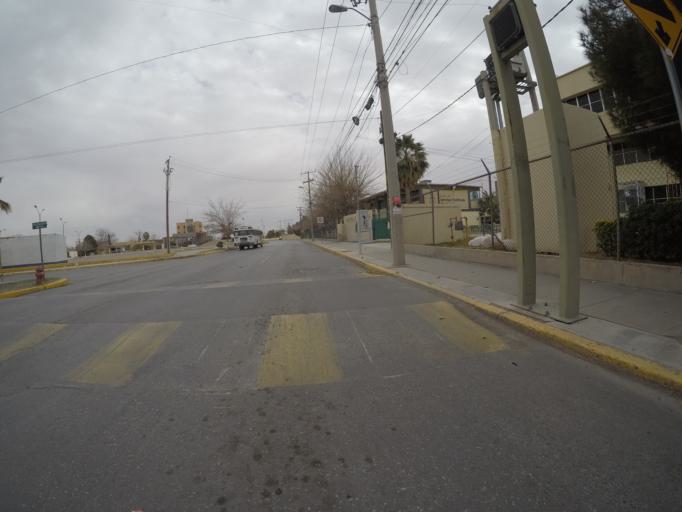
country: MX
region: Chihuahua
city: Ciudad Juarez
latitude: 31.7411
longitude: -106.4451
